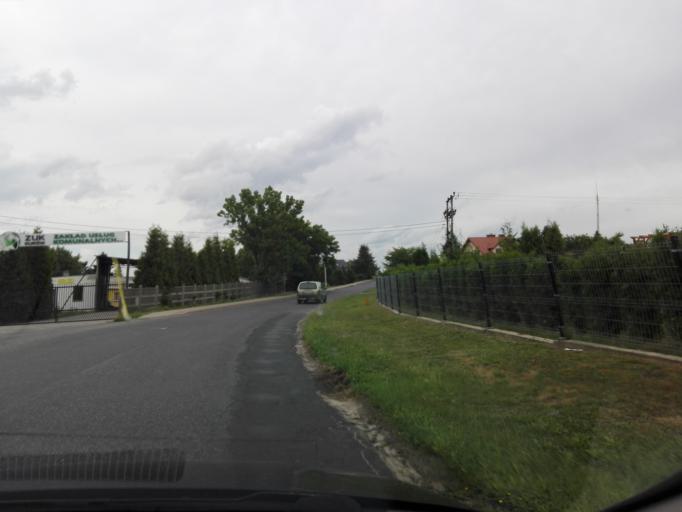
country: PL
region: Lublin Voivodeship
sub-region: Powiat pulawski
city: Kurow
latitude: 51.3932
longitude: 22.1919
